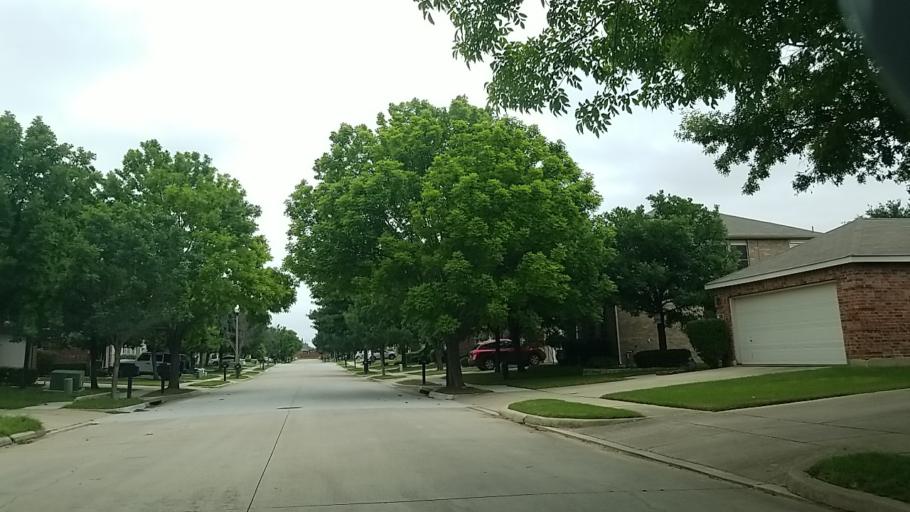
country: US
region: Texas
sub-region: Denton County
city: Corinth
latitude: 33.1682
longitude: -97.0733
